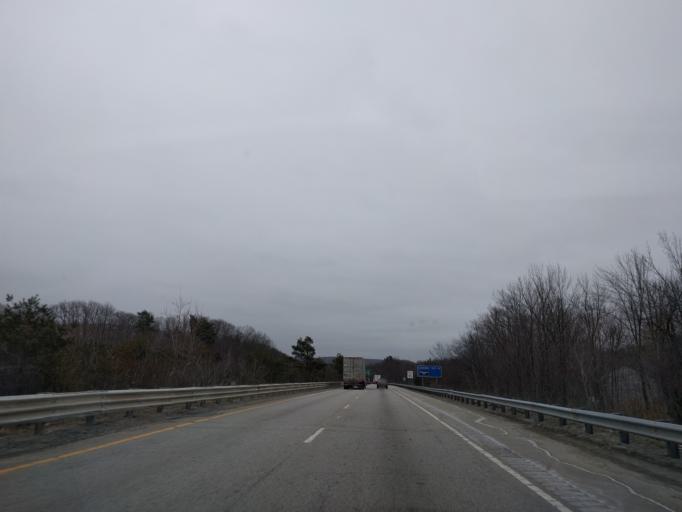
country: US
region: Massachusetts
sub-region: Worcester County
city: Westminster
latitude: 42.5488
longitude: -71.9094
